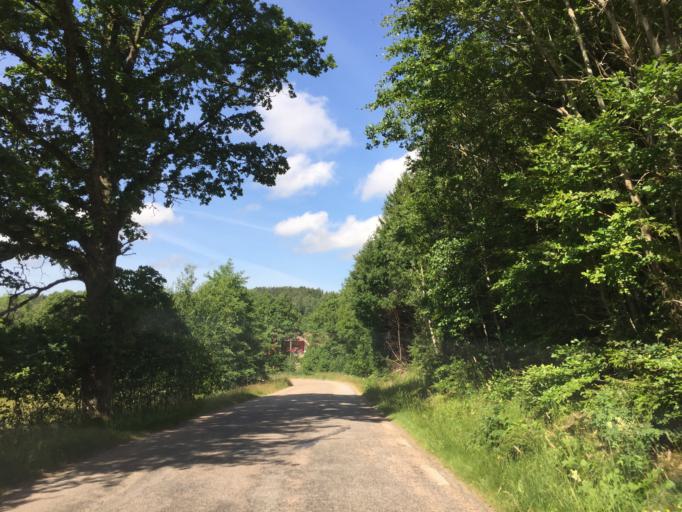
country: SE
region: Vaestra Goetaland
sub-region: Orust
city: Henan
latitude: 58.2924
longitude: 11.6382
